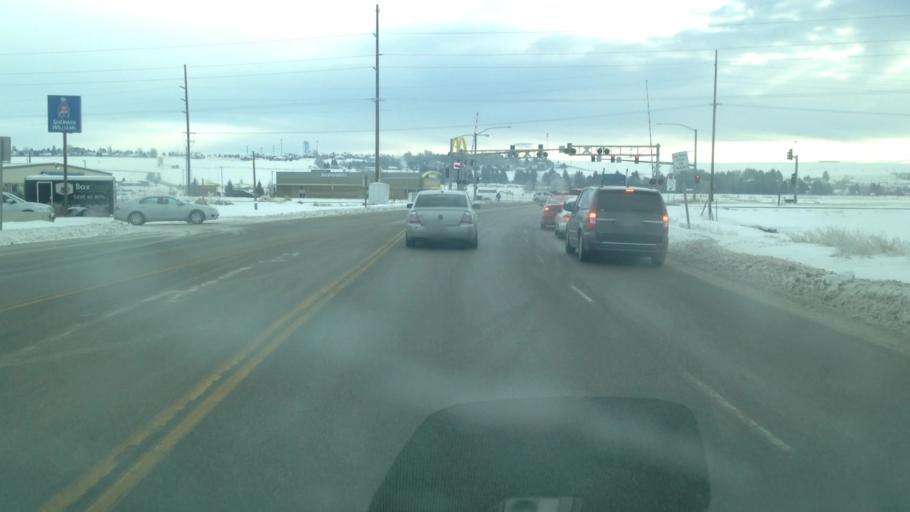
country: US
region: Idaho
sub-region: Madison County
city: Rexburg
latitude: 43.8044
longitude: -111.8103
